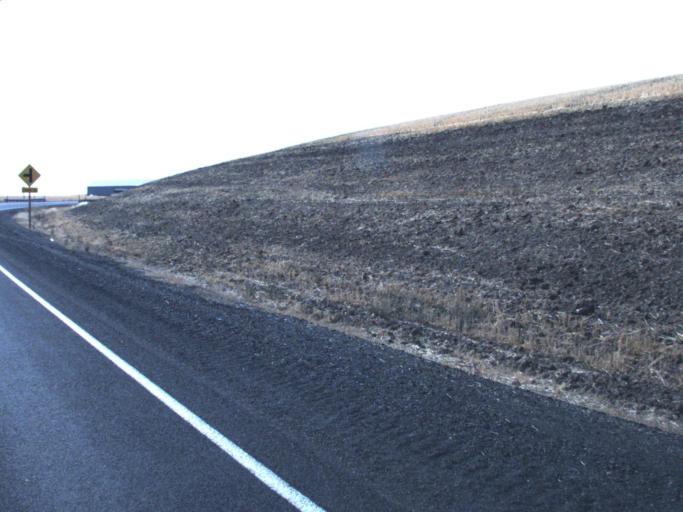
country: US
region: Washington
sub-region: Whitman County
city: Pullman
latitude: 46.8289
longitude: -117.1148
